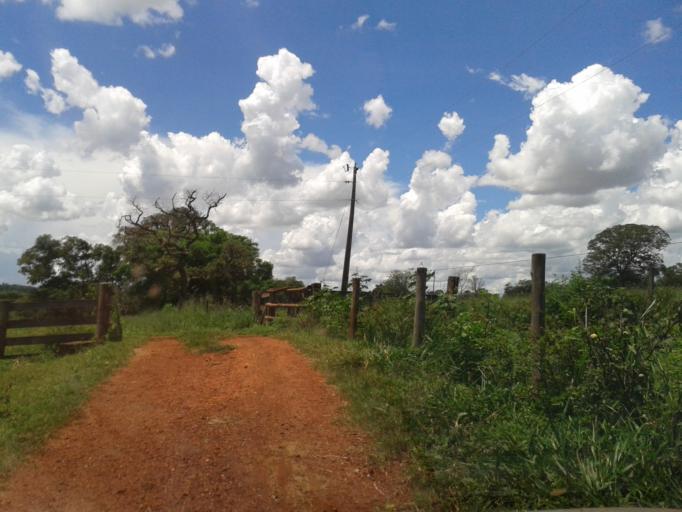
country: BR
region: Minas Gerais
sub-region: Santa Vitoria
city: Santa Vitoria
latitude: -18.7950
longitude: -49.8374
